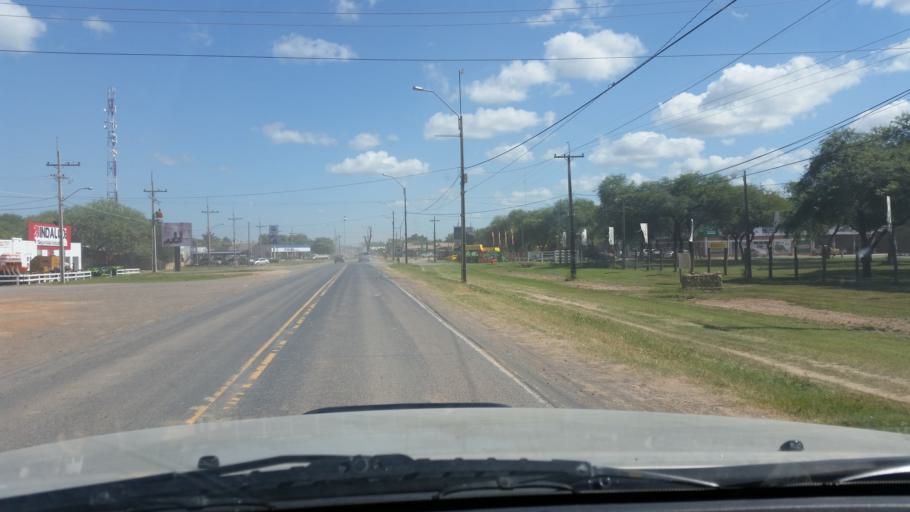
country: PY
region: Boqueron
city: Colonia Menno
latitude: -22.3909
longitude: -59.8364
